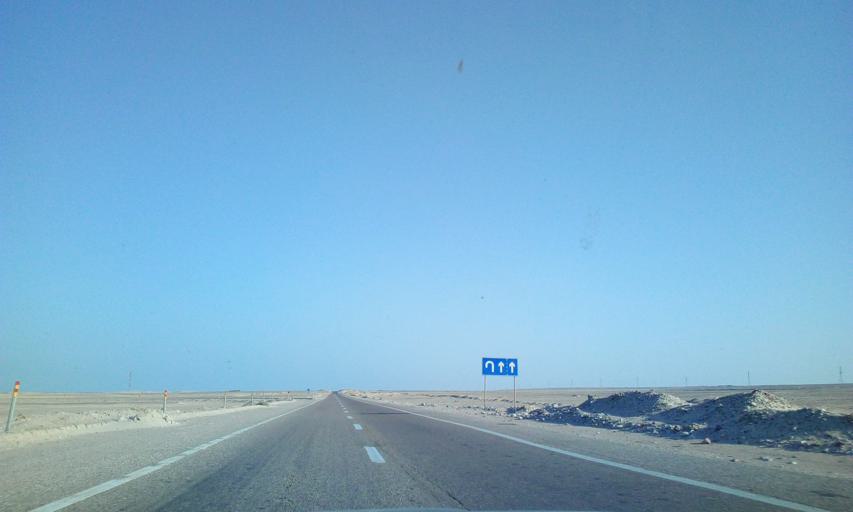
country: EG
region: As Suways
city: Ain Sukhna
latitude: 28.7982
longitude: 32.7425
